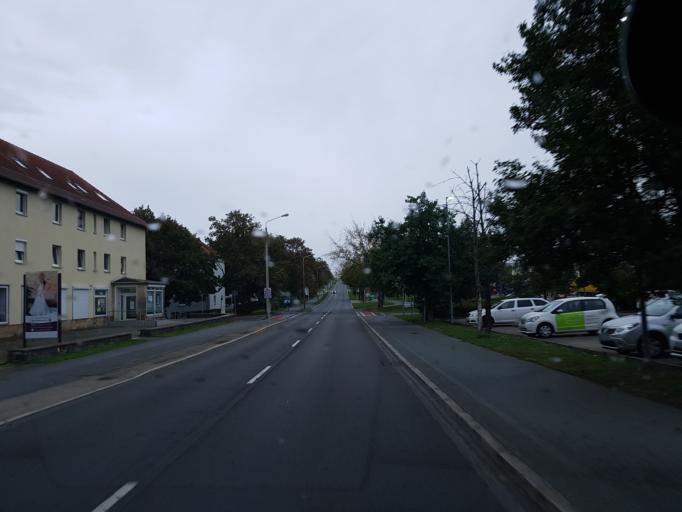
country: DE
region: Saxony
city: Riesa
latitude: 51.2980
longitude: 13.2996
